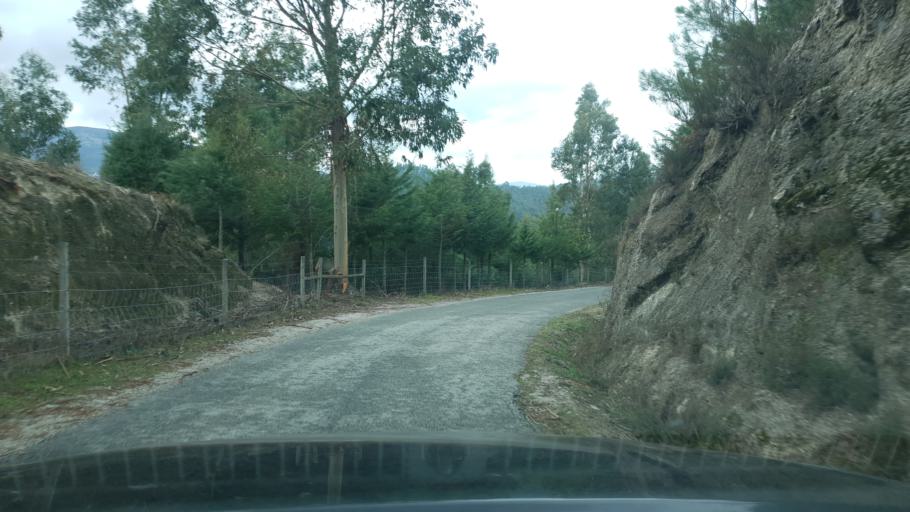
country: PT
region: Viseu
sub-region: Castro Daire
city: Castro Daire
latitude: 40.8787
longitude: -7.9934
